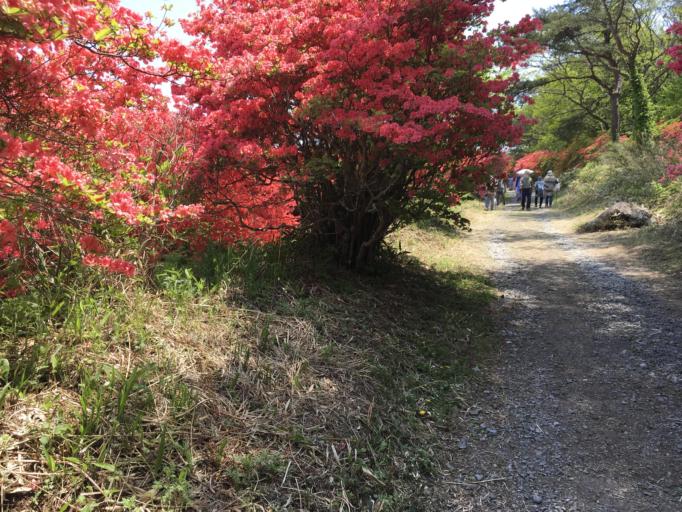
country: JP
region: Iwate
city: Ofunato
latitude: 38.8534
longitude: 141.4702
